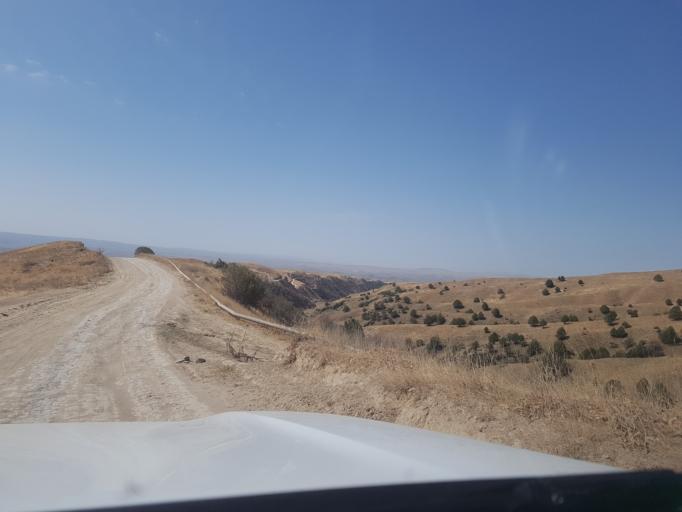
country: TM
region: Ahal
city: Baharly
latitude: 38.2816
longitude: 56.9248
